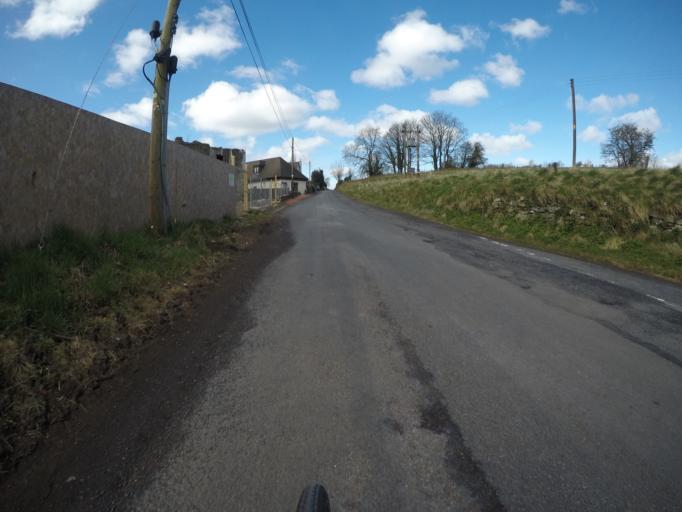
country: GB
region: Scotland
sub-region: East Ayrshire
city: Crosshouse
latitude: 55.6023
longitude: -4.5682
